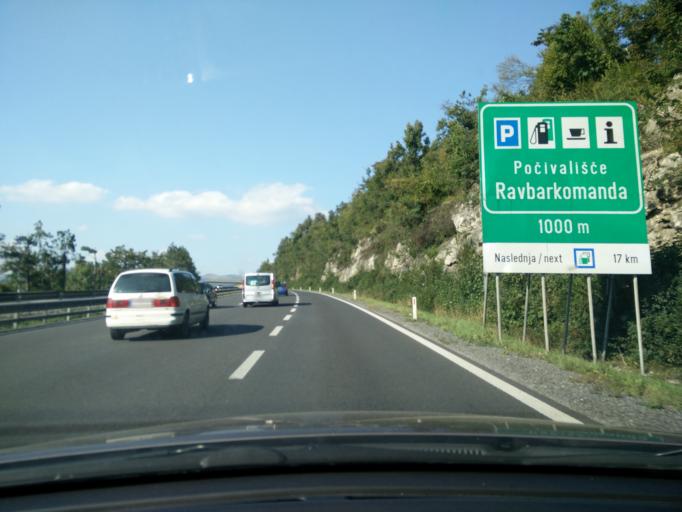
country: SI
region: Postojna
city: Postojna
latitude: 45.7722
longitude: 14.2227
